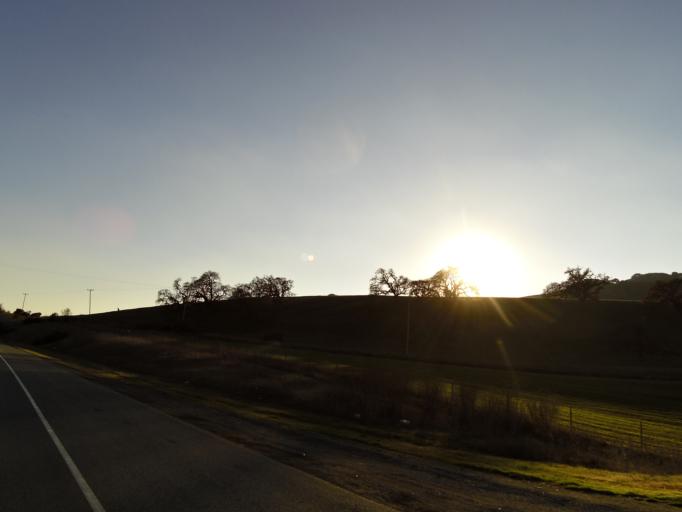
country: US
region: California
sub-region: Santa Clara County
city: Gilroy
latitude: 36.9368
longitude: -121.5527
